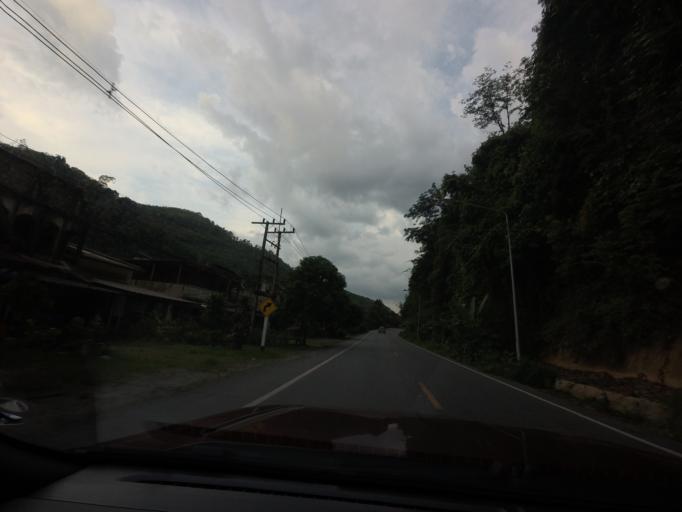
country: TH
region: Yala
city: Than To
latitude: 6.0060
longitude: 101.1944
